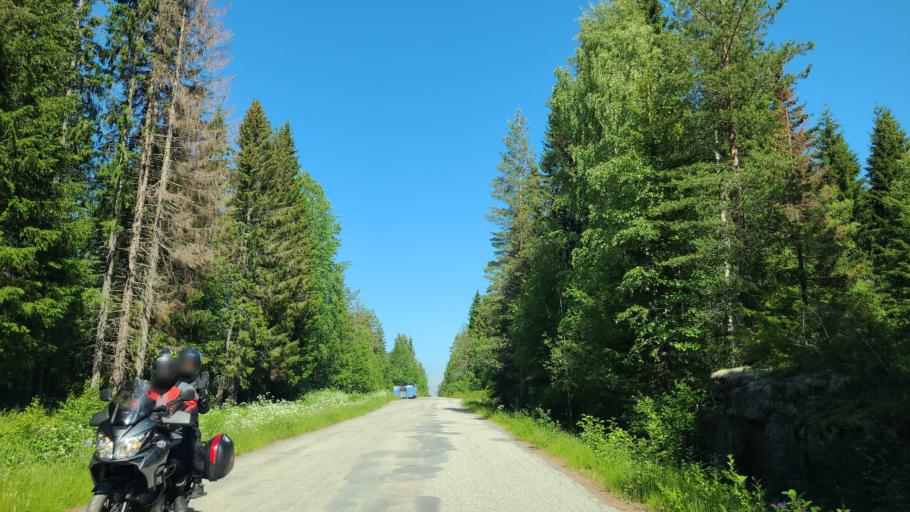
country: SE
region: Vaesternorrland
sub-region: OErnskoeldsviks Kommun
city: Husum
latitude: 63.4165
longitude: 19.2210
